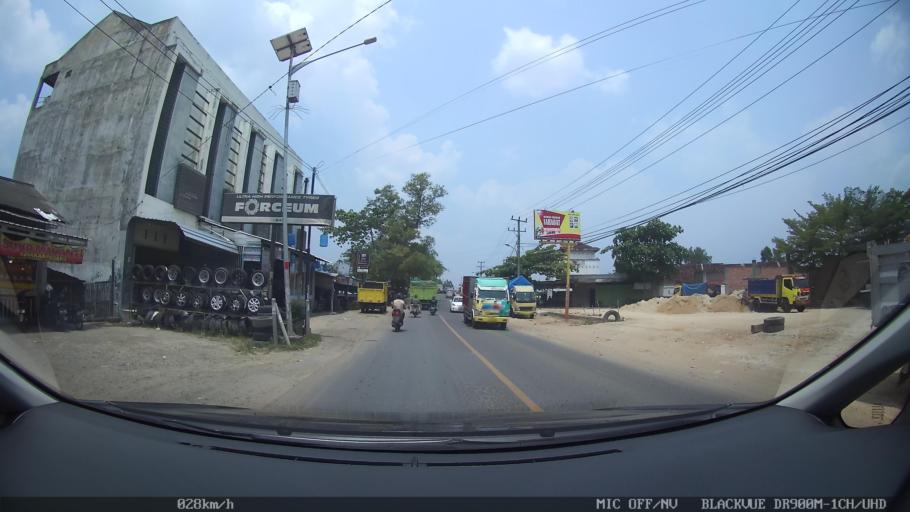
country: ID
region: Lampung
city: Pringsewu
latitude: -5.3632
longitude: 105.0010
